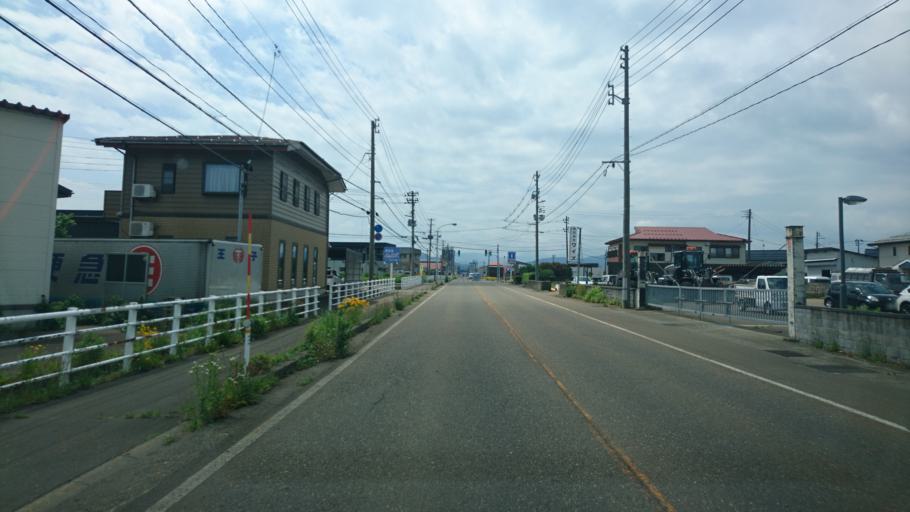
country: JP
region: Niigata
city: Arai
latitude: 37.0675
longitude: 138.2578
